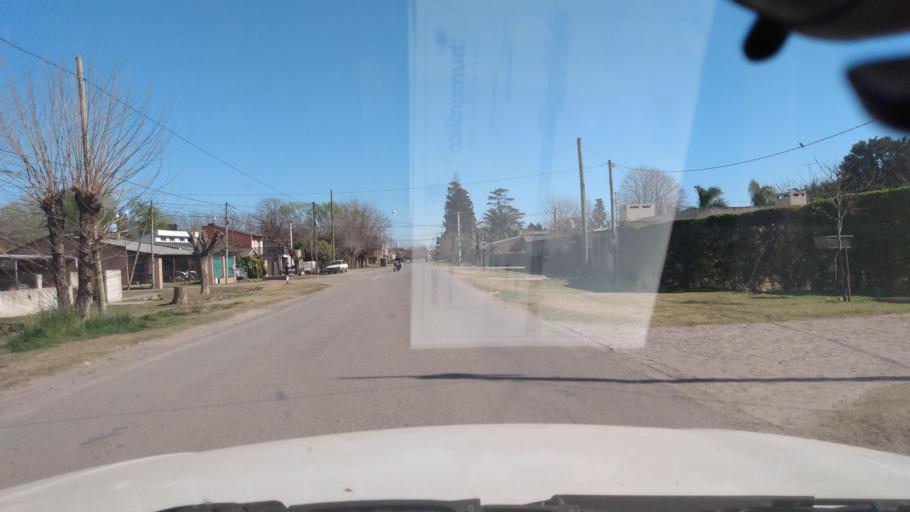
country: AR
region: Buenos Aires
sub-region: Partido de Mercedes
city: Mercedes
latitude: -34.6580
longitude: -59.4064
